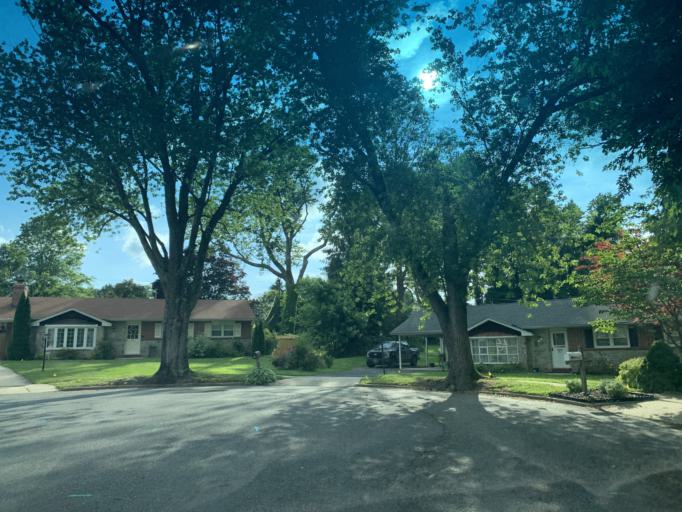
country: US
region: Maryland
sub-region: Harford County
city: South Bel Air
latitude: 39.5336
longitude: -76.3400
